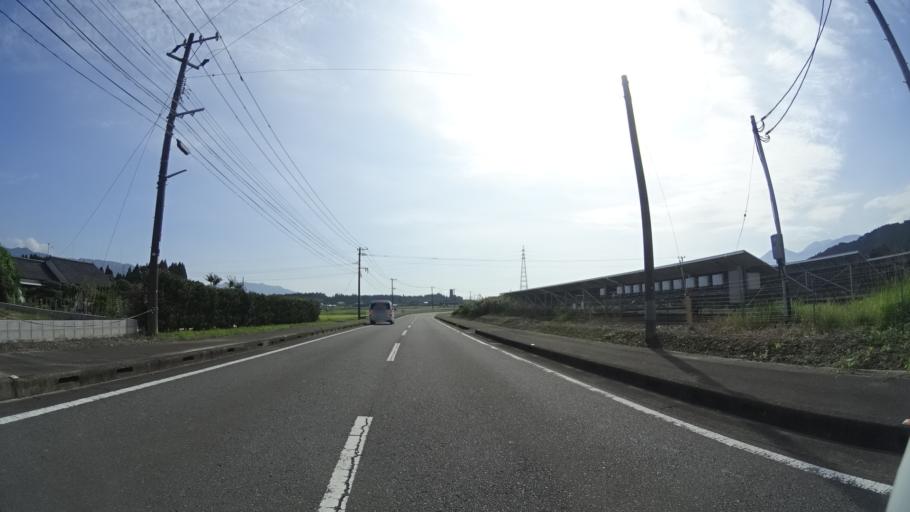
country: JP
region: Kagoshima
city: Okuchi-shinohara
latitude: 32.0425
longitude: 130.7810
